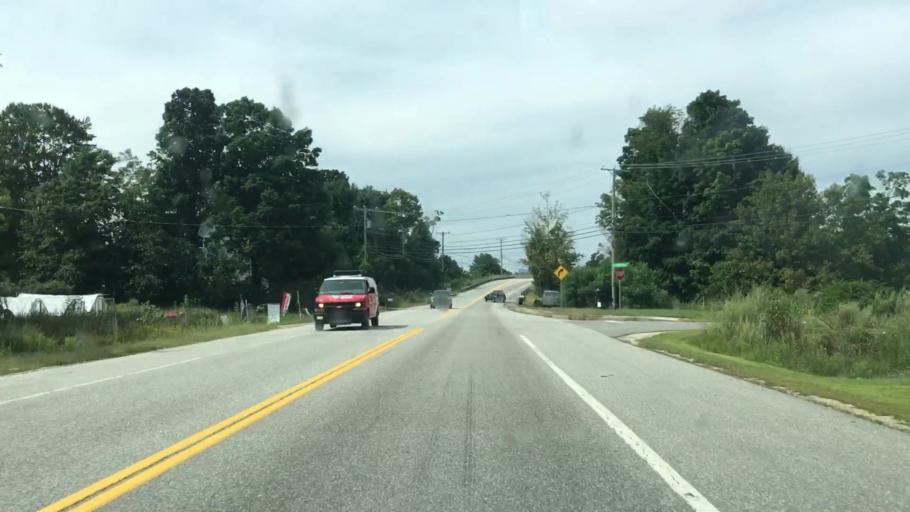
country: US
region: New Hampshire
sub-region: Strafford County
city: Dover
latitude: 43.1856
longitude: -70.8949
